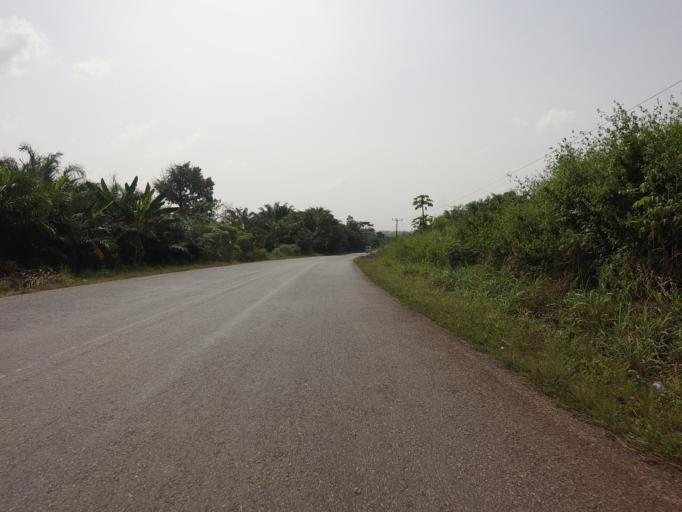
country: GH
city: Akropong
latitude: 6.2701
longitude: 0.1360
